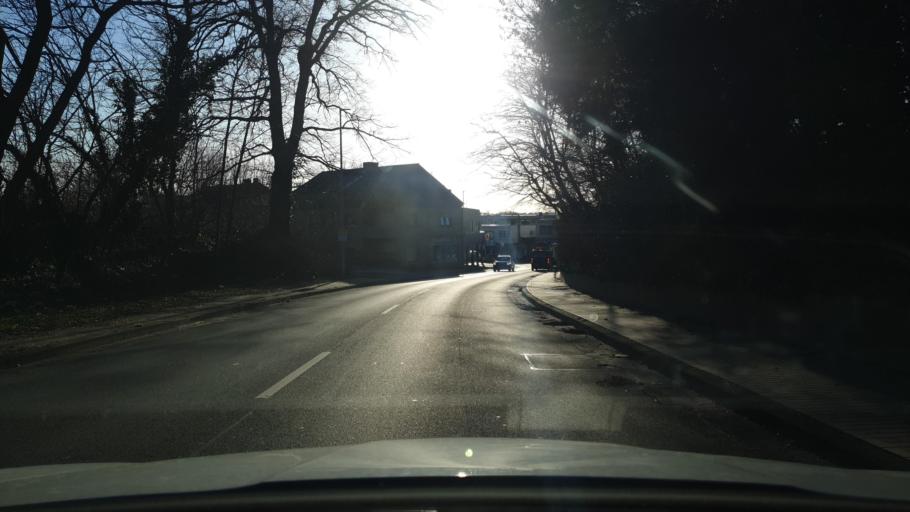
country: DE
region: North Rhine-Westphalia
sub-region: Regierungsbezirk Detmold
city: Kirchlengern
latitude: 52.1991
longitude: 8.6441
